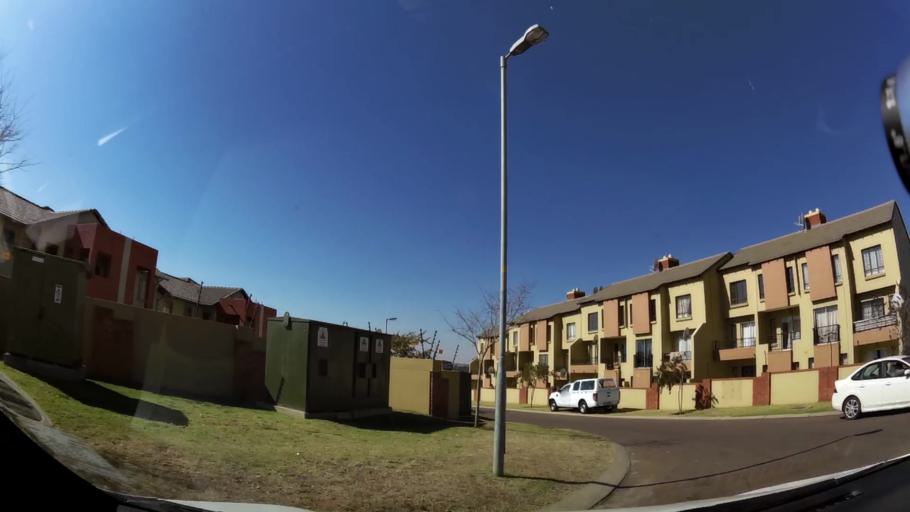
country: ZA
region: Gauteng
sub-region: City of Johannesburg Metropolitan Municipality
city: Midrand
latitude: -25.9505
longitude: 28.1011
